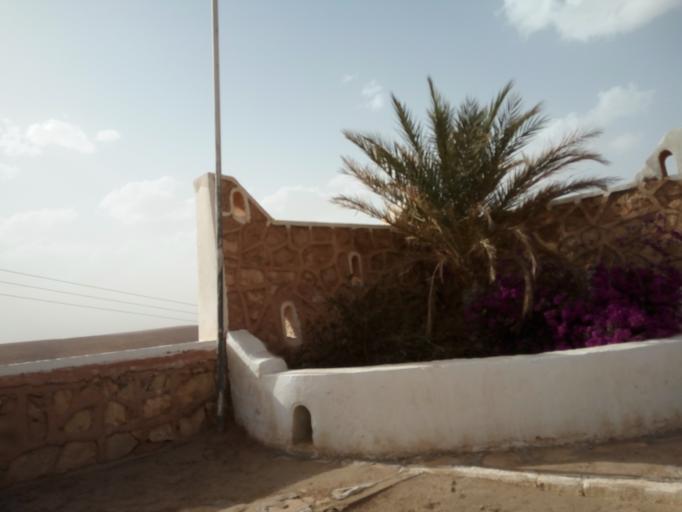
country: DZ
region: Ghardaia
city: Ghardaia
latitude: 32.4637
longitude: 3.6896
